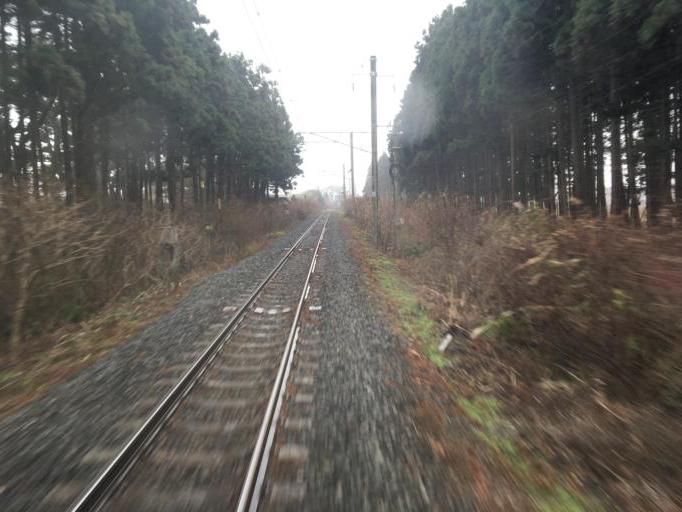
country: JP
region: Aomori
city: Aomori Shi
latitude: 40.9848
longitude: 140.6533
